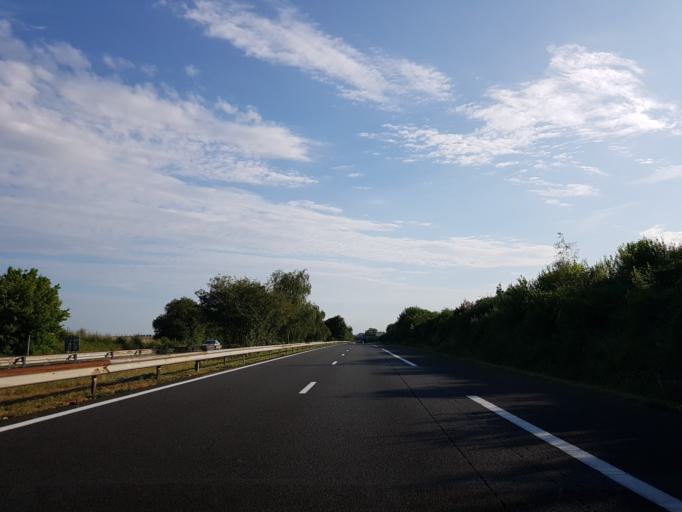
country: FR
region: Picardie
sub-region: Departement de la Somme
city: Moislains
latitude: 50.0265
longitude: 2.8895
